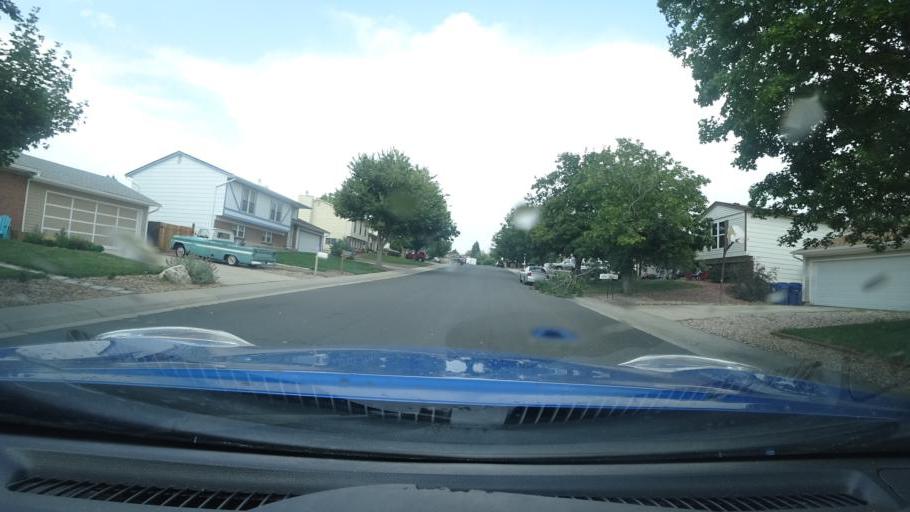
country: US
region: Colorado
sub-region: Adams County
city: Aurora
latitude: 39.6941
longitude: -104.7679
